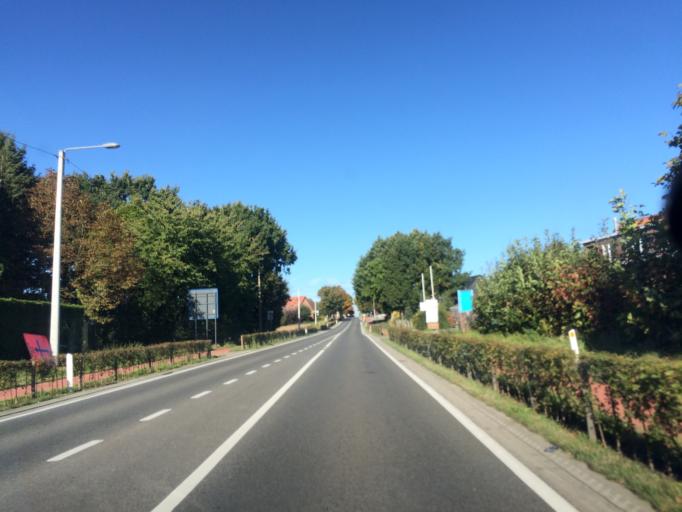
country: BE
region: Flanders
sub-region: Provincie Vlaams-Brabant
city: Merchtem
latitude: 50.9279
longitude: 4.2622
